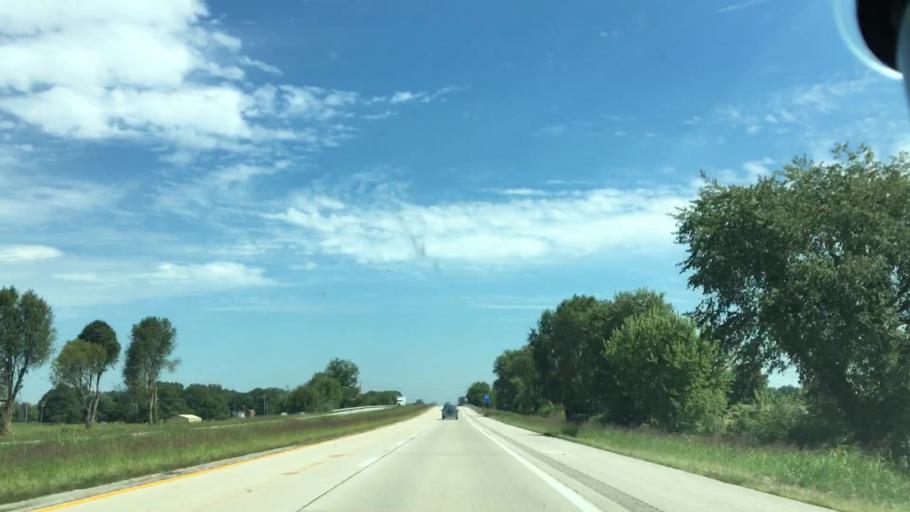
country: US
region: Kentucky
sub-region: Daviess County
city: Owensboro
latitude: 37.7666
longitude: -87.1819
